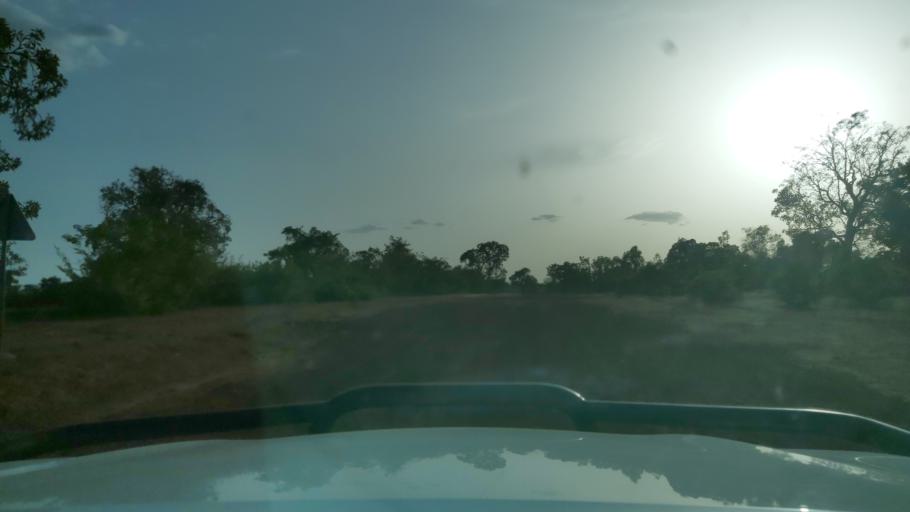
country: ML
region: Koulikoro
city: Kolokani
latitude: 13.2047
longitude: -7.9211
